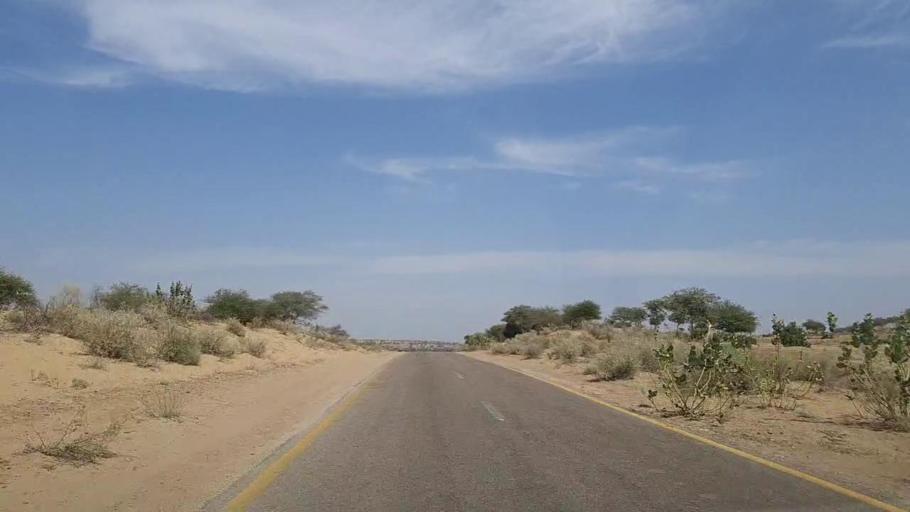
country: PK
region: Sindh
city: Mithi
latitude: 24.8119
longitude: 69.8175
